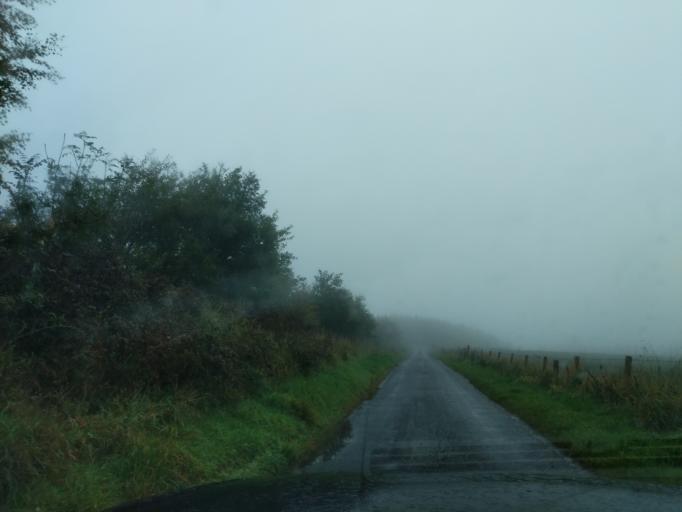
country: GB
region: Scotland
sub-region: East Lothian
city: Dunbar
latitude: 55.9378
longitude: -2.4232
